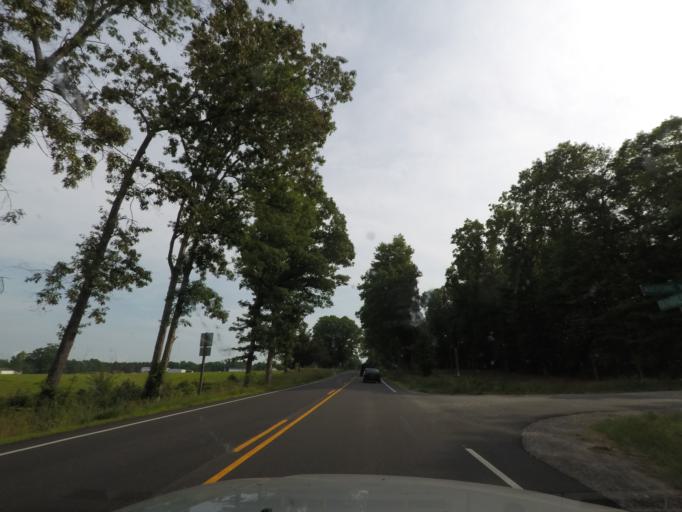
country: US
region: Virginia
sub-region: Prince Edward County
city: Hampden Sydney
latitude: 37.1476
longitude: -78.4415
